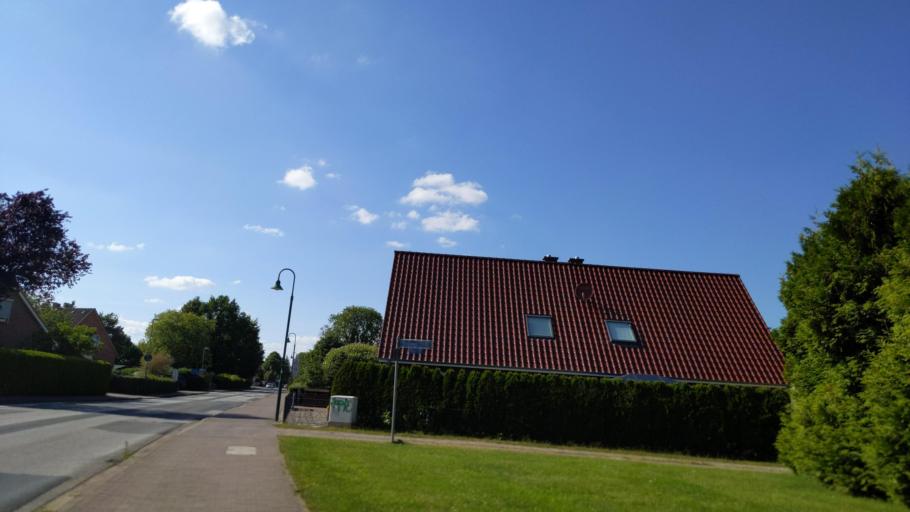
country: DE
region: Schleswig-Holstein
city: Krummesse
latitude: 53.7778
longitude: 10.6455
